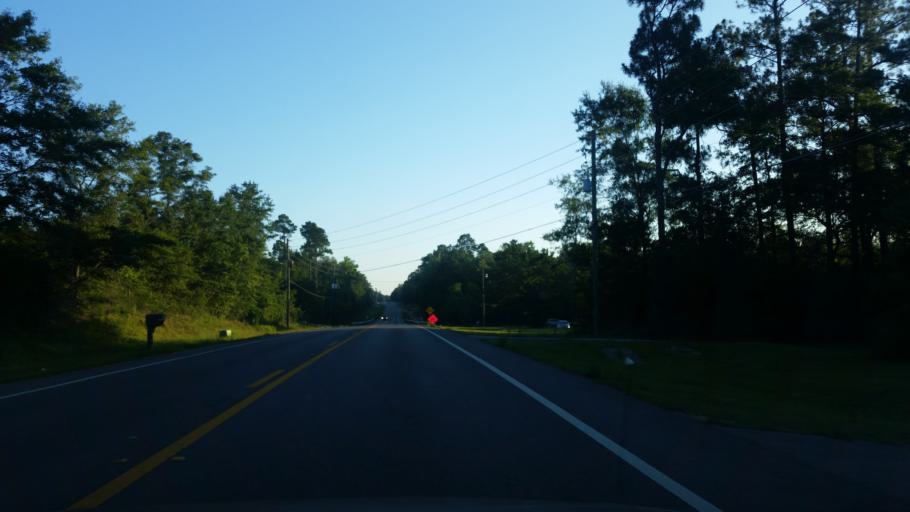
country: US
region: Florida
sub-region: Escambia County
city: Cantonment
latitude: 30.5812
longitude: -87.3283
